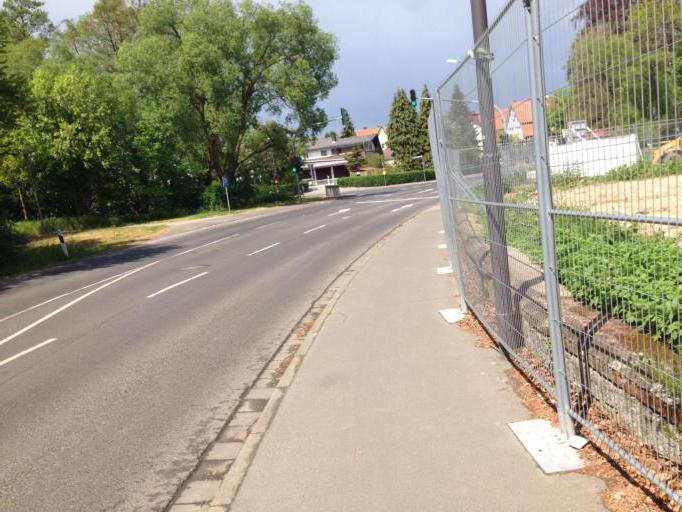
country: DE
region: Hesse
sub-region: Regierungsbezirk Giessen
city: Alsfeld
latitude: 50.7438
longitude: 9.2720
